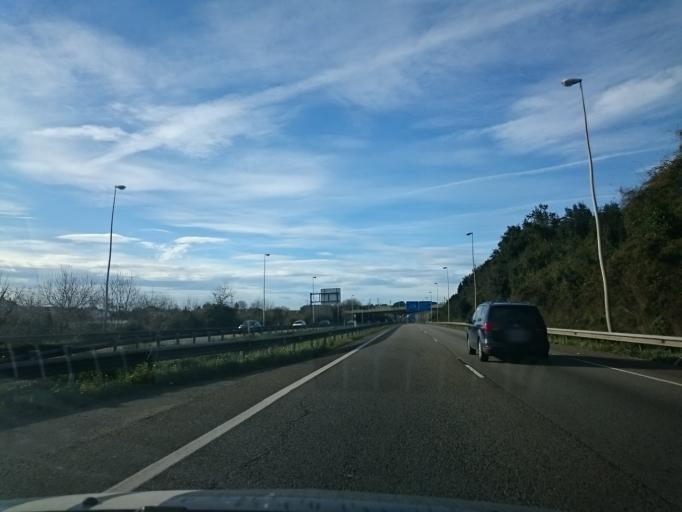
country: ES
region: Asturias
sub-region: Province of Asturias
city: Gijon
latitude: 43.5132
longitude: -5.6726
